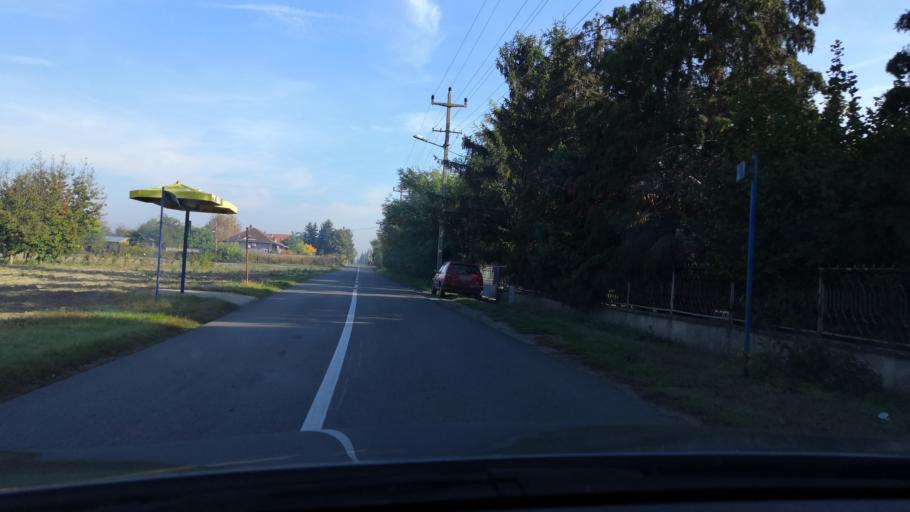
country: HU
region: Csongrad
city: Asotthalom
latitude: 46.1133
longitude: 19.8398
